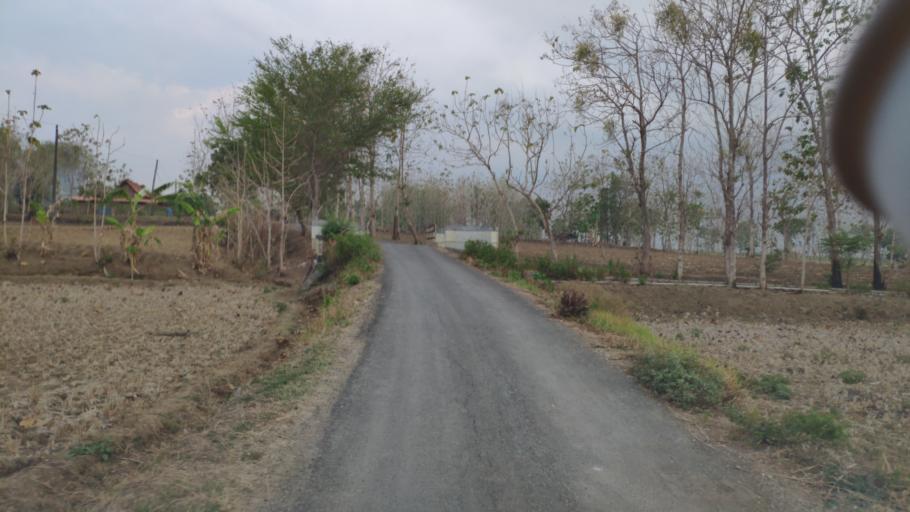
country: ID
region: Central Java
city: Bogorejo
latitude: -6.9407
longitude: 111.3371
